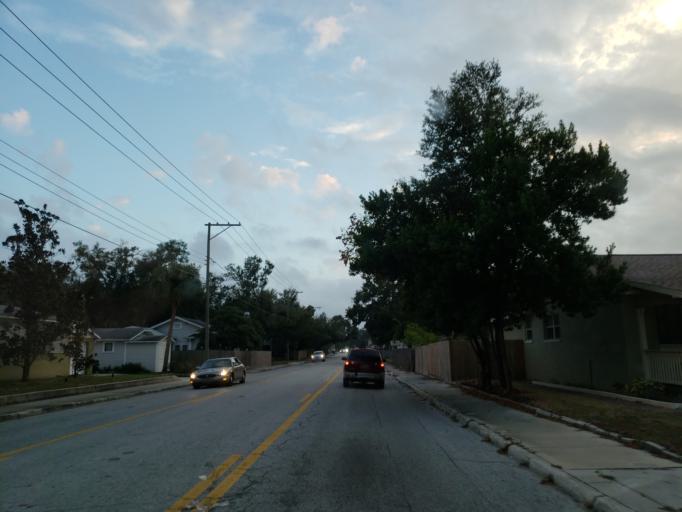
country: US
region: Florida
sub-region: Hillsborough County
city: Tampa
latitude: 27.9953
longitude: -82.4621
